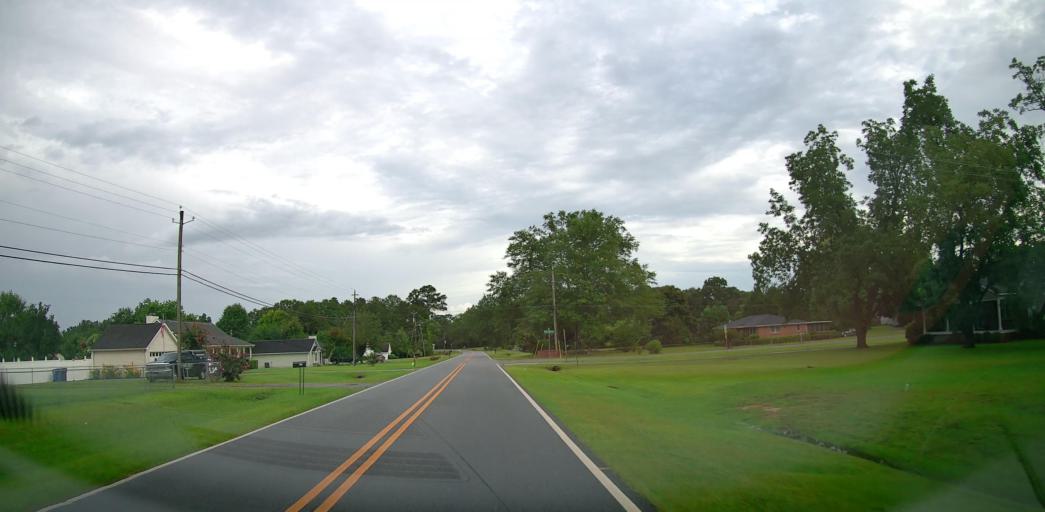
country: US
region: Georgia
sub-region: Peach County
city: Byron
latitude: 32.7393
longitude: -83.7049
